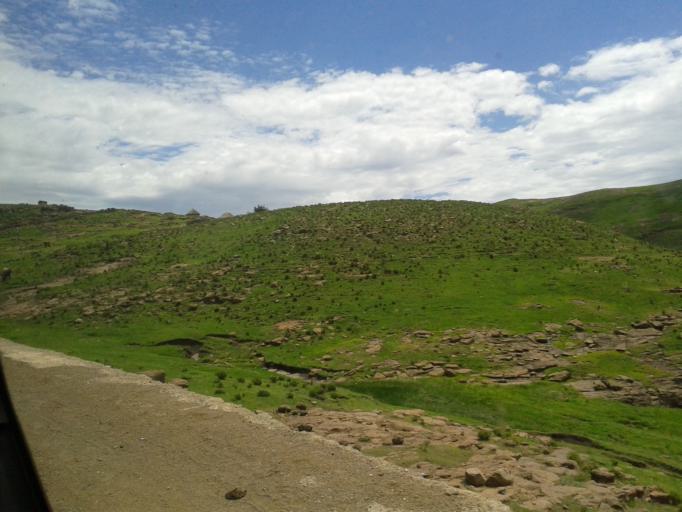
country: LS
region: Maseru
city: Nako
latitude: -29.8559
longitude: 28.0327
